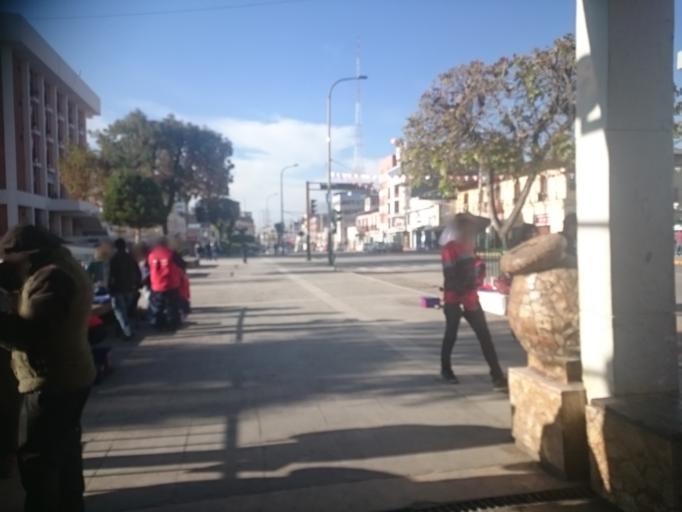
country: PE
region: Junin
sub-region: Provincia de Huancayo
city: Huancayo
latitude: -12.0708
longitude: -75.2089
